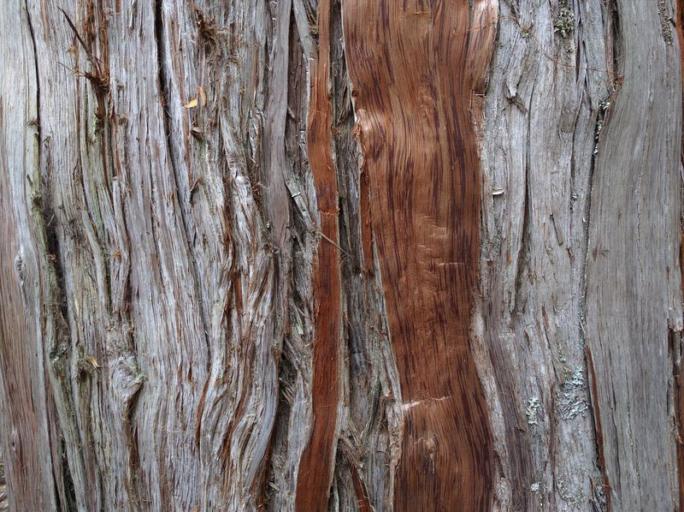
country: AR
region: Chubut
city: Trevelin
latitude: -42.7505
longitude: -71.7537
